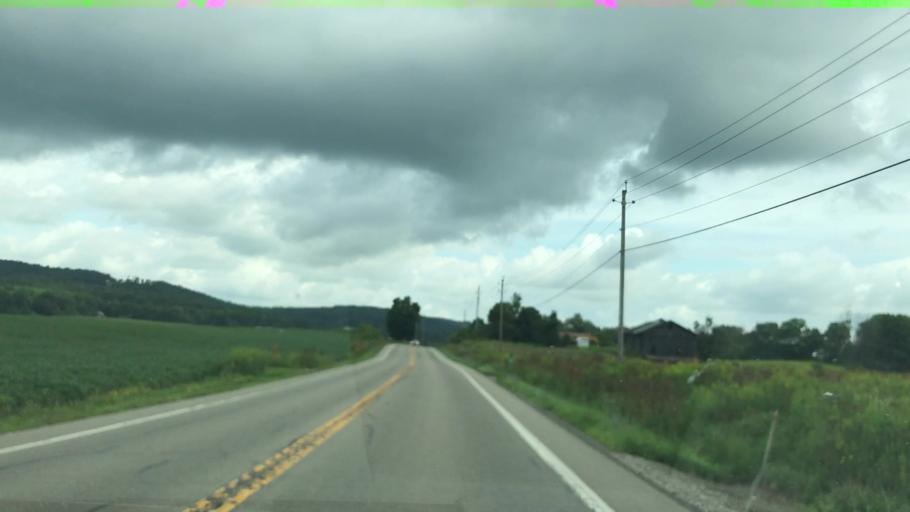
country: US
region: New York
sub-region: Steuben County
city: Bath
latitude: 42.4211
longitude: -77.3387
